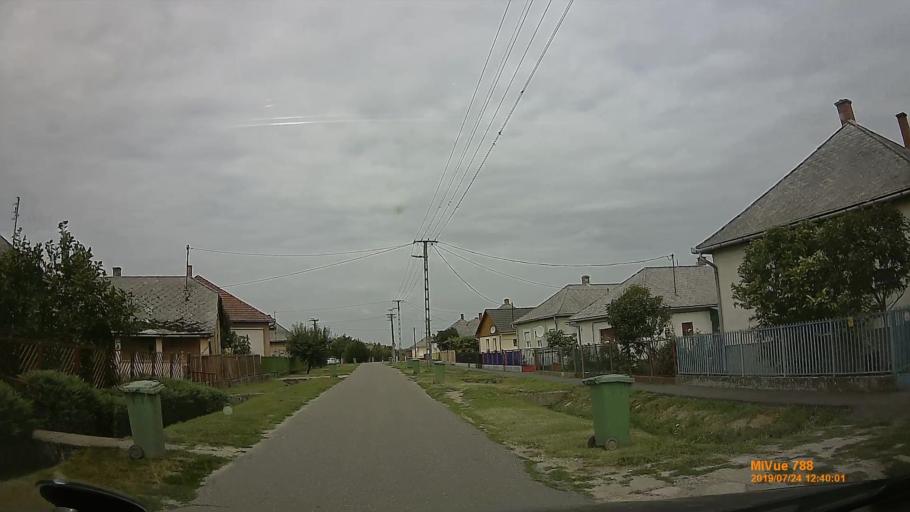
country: HU
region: Szabolcs-Szatmar-Bereg
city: Aranyosapati
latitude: 48.1896
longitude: 22.3129
